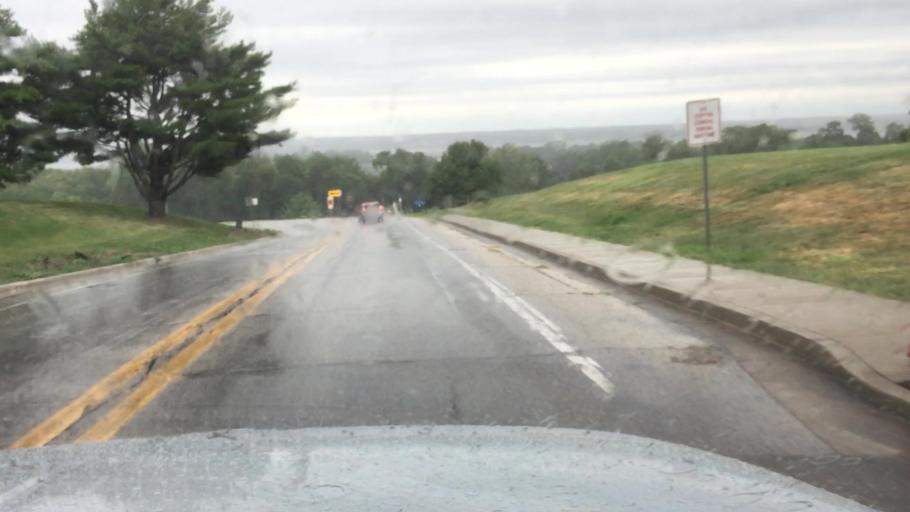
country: US
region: Illinois
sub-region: Hancock County
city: Nauvoo
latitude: 40.5498
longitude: -91.3852
